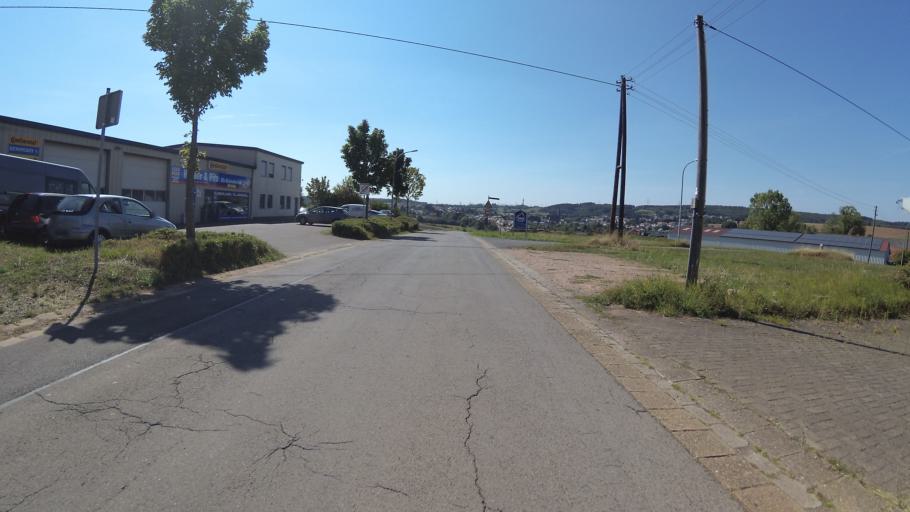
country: DE
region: Saarland
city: Illingen
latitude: 49.3762
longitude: 7.0387
